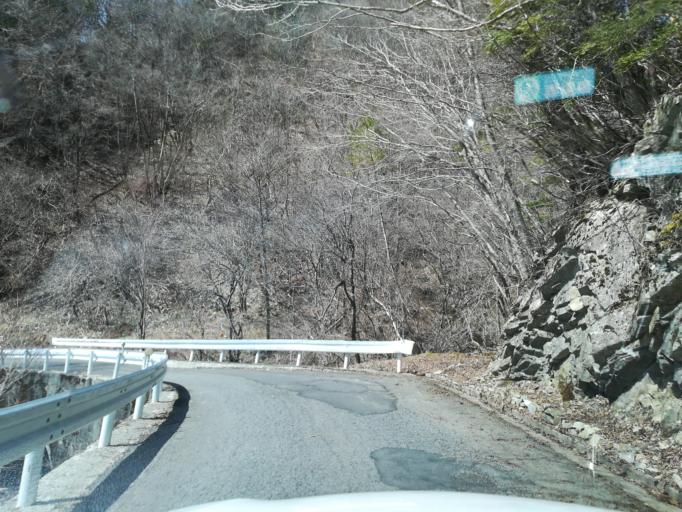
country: JP
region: Tokushima
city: Wakimachi
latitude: 33.8671
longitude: 134.0811
